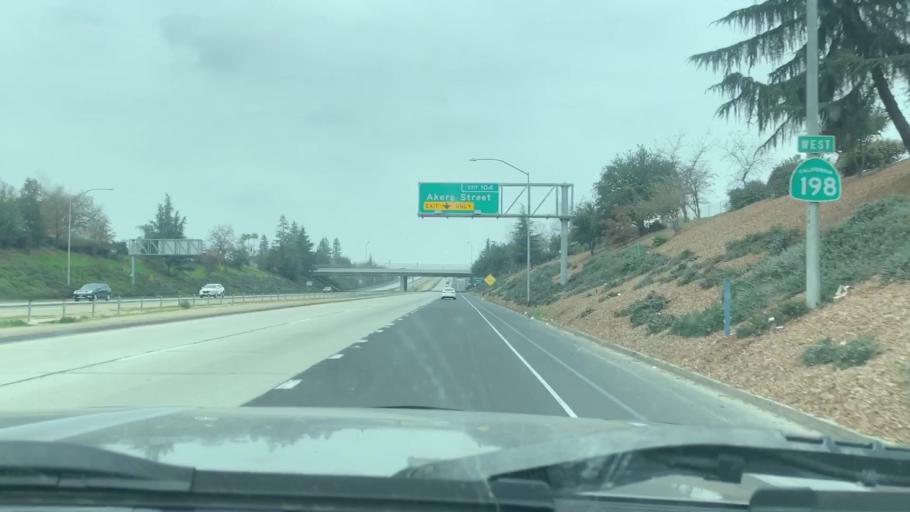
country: US
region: California
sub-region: Tulare County
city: Visalia
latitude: 36.3276
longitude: -119.3379
